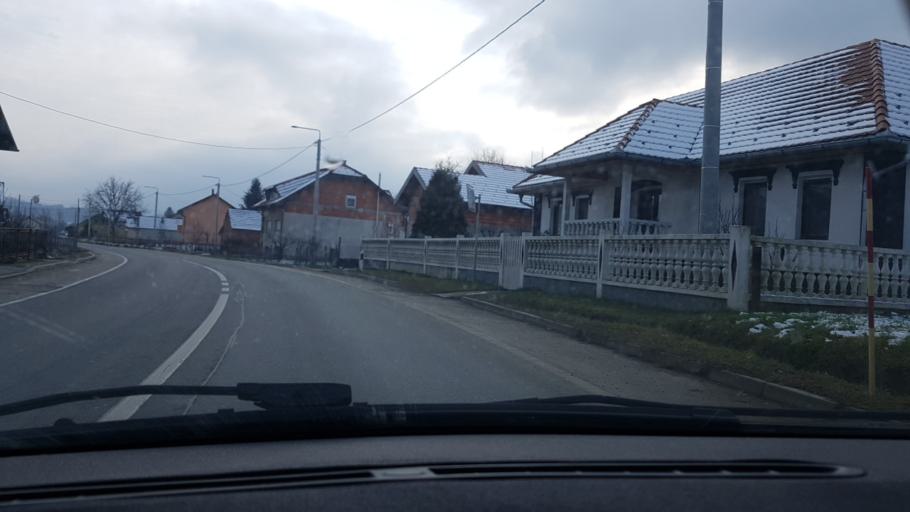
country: HR
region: Varazdinska
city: Tuzno
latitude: 46.2760
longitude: 16.2070
